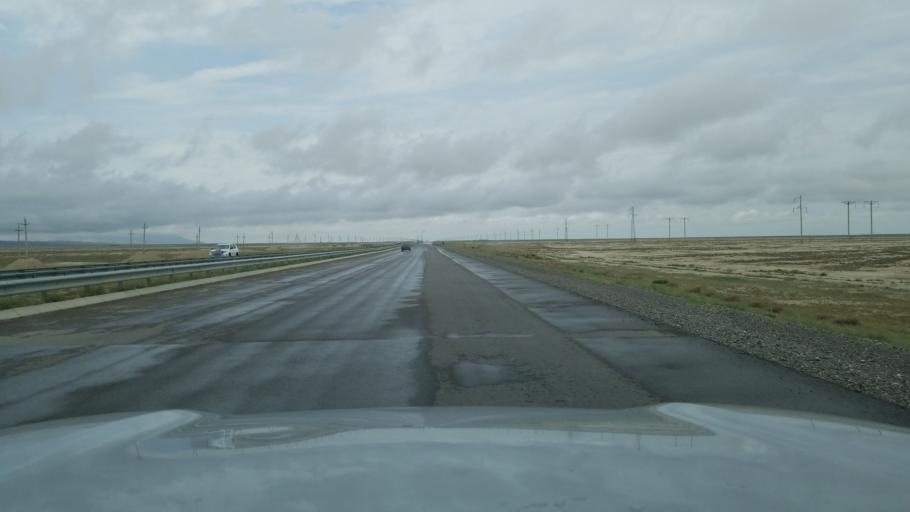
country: TM
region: Balkan
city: Serdar
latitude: 39.1226
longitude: 55.9038
